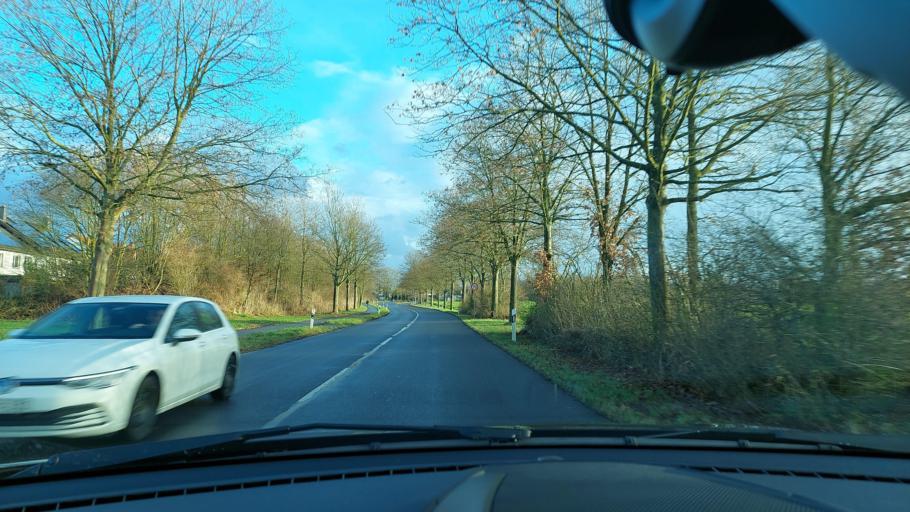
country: DE
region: North Rhine-Westphalia
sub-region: Regierungsbezirk Dusseldorf
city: Dormagen
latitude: 51.0699
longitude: 6.8021
